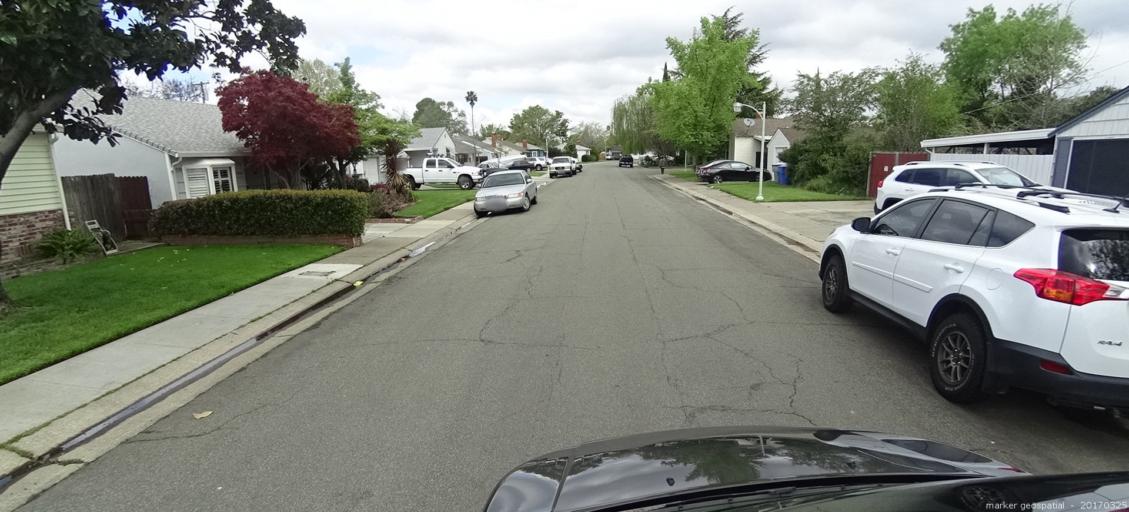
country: US
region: California
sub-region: Sacramento County
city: Parkway
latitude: 38.5229
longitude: -121.4388
